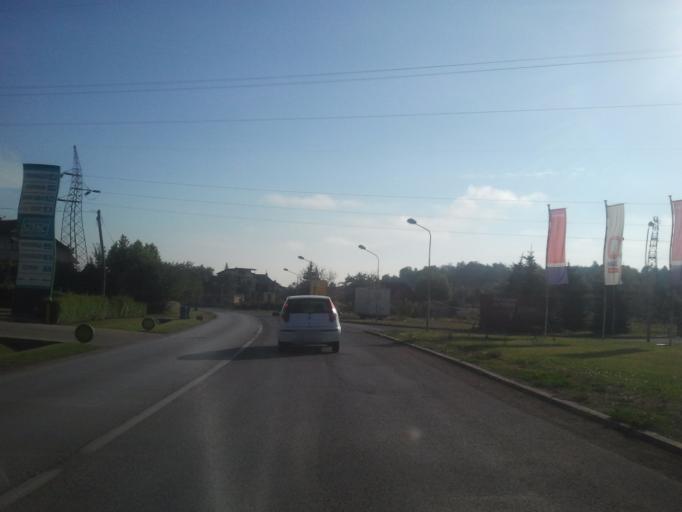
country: RS
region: Autonomna Pokrajina Vojvodina
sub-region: Juznobacki Okrug
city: Petrovaradin
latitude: 45.2297
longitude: 19.8829
